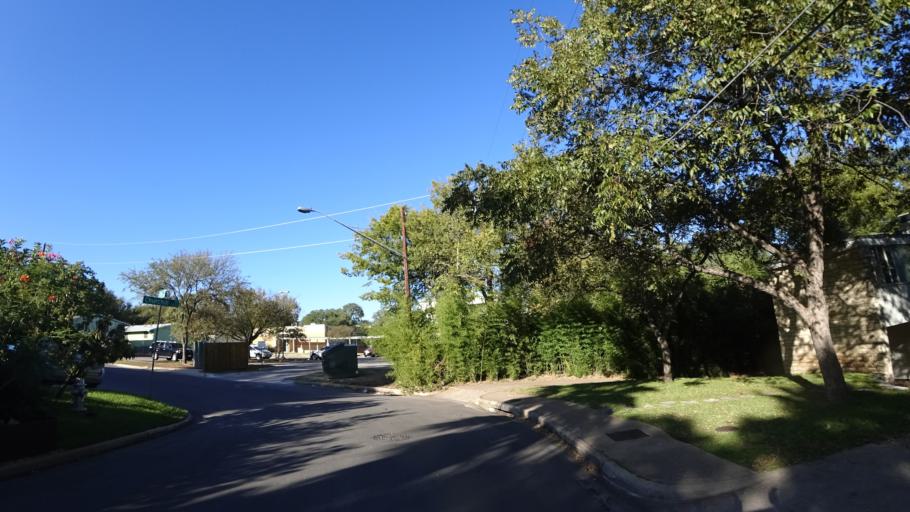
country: US
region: Texas
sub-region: Travis County
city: Austin
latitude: 30.3042
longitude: -97.7511
